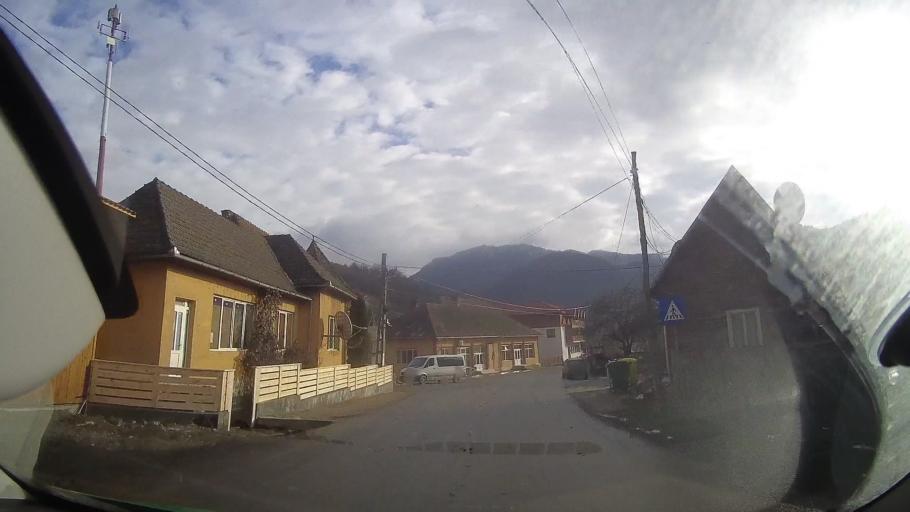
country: RO
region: Alba
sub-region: Comuna Ocolis
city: Ocolis
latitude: 46.4792
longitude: 23.4649
